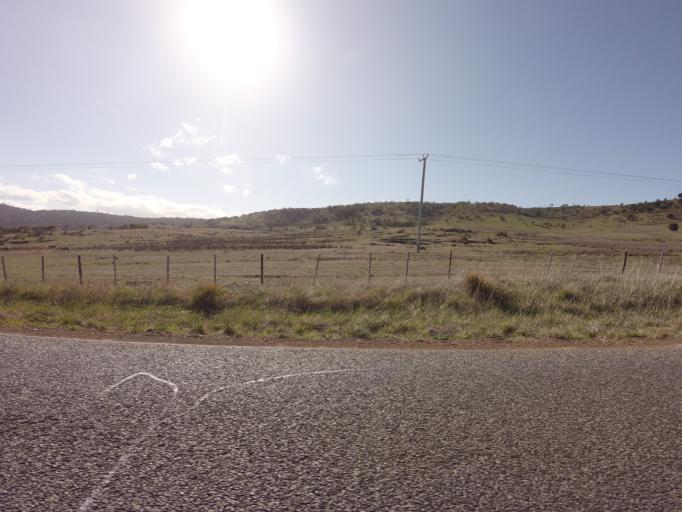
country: AU
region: Tasmania
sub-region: Sorell
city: Sorell
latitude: -42.1956
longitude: 148.0538
